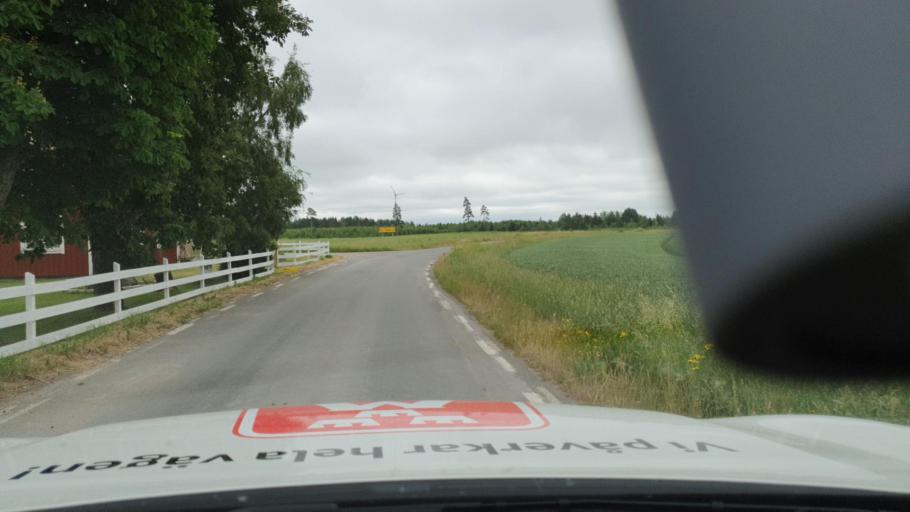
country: SE
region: Vaestra Goetaland
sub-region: Tibro Kommun
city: Tibro
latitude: 58.3833
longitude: 14.1196
